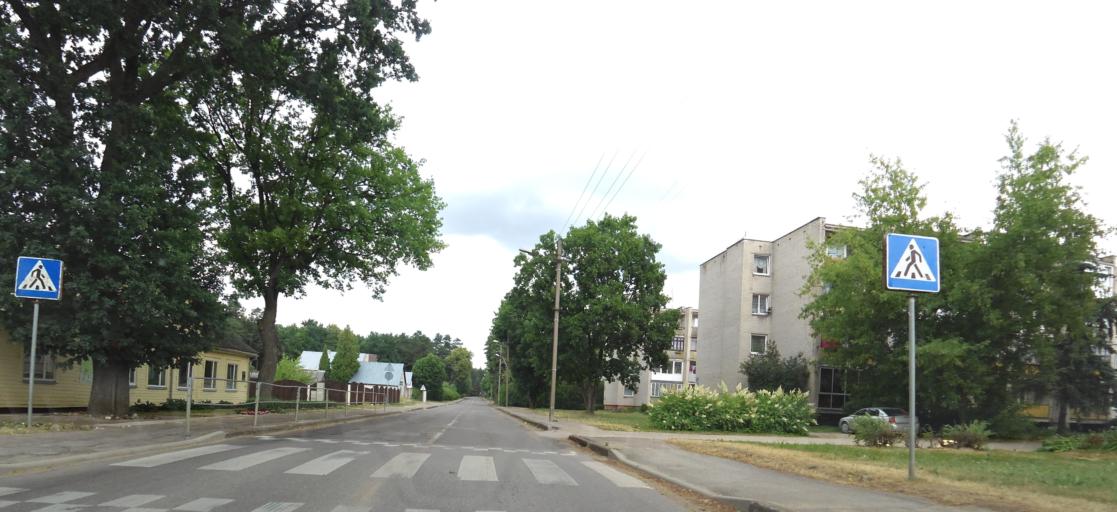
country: LT
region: Vilnius County
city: Ukmerge
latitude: 55.2150
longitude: 24.7880
